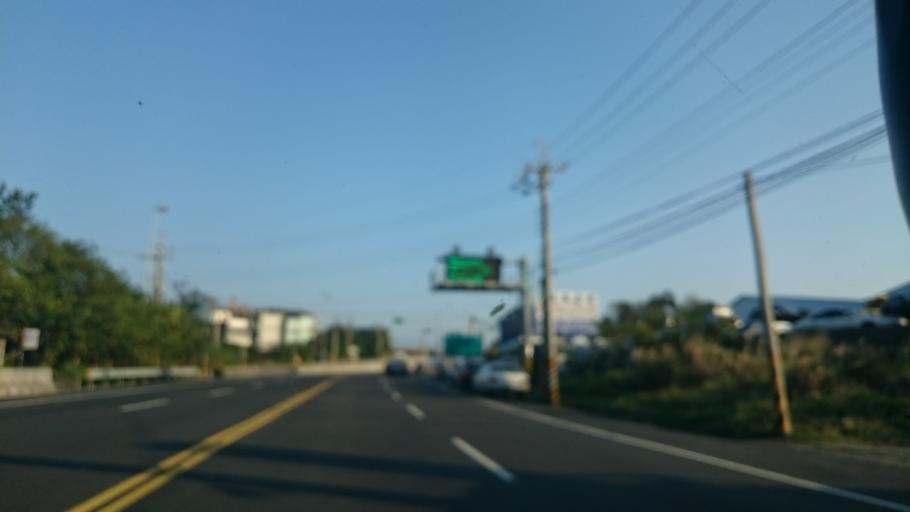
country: TW
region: Taiwan
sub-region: Miaoli
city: Miaoli
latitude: 24.6002
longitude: 120.7827
